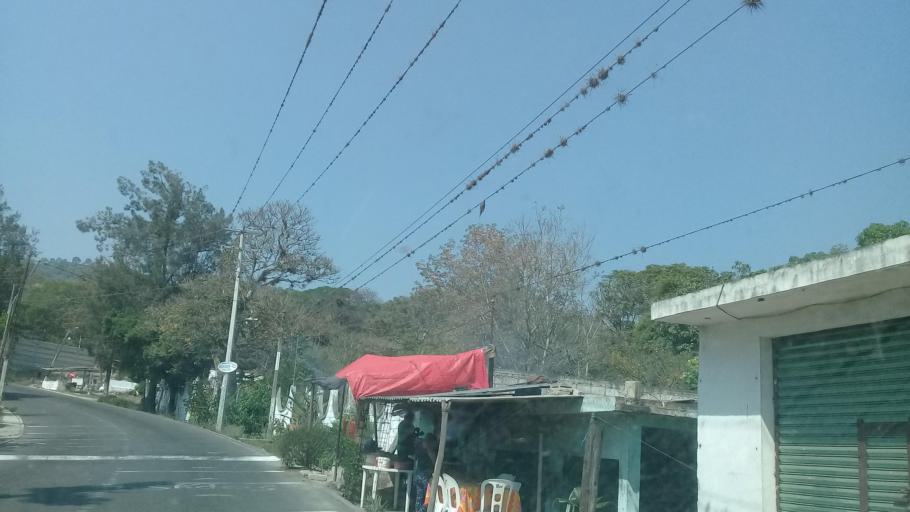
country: MX
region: Veracruz
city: El Castillo
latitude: 19.5716
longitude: -96.8351
